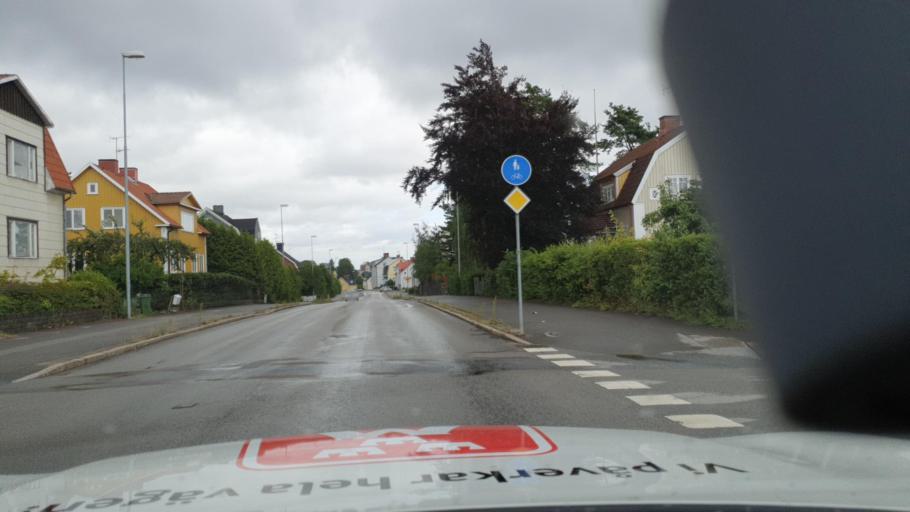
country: SE
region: Vaestra Goetaland
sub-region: Amals Kommun
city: Amal
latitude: 59.0539
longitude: 12.6905
